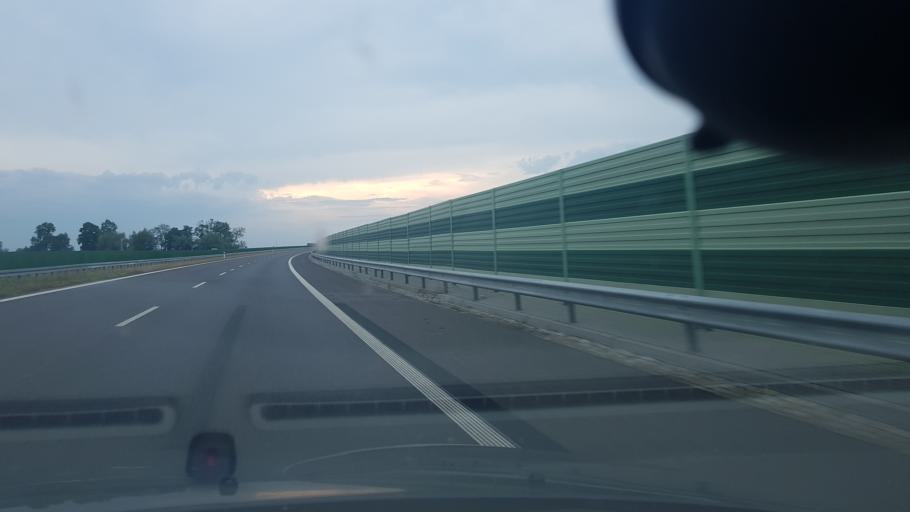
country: PL
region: Pomeranian Voivodeship
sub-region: Powiat nowodworski
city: Nowy Dwor Gdanski
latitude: 54.1765
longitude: 19.1889
